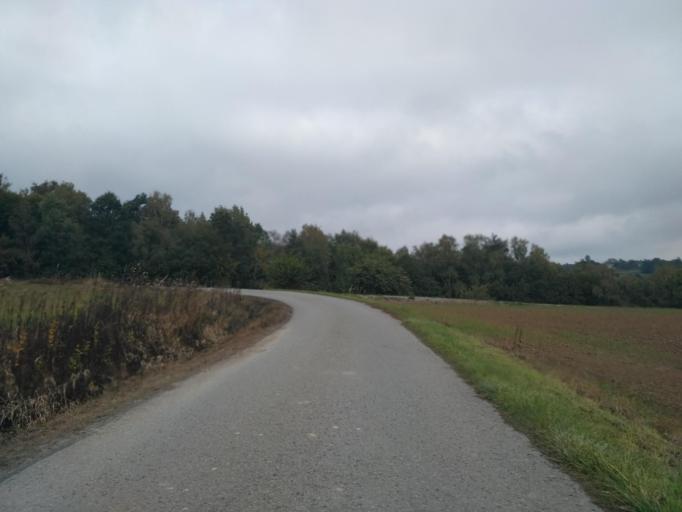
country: PL
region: Subcarpathian Voivodeship
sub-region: Powiat debicki
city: Brzostek
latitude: 49.9475
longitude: 21.4450
